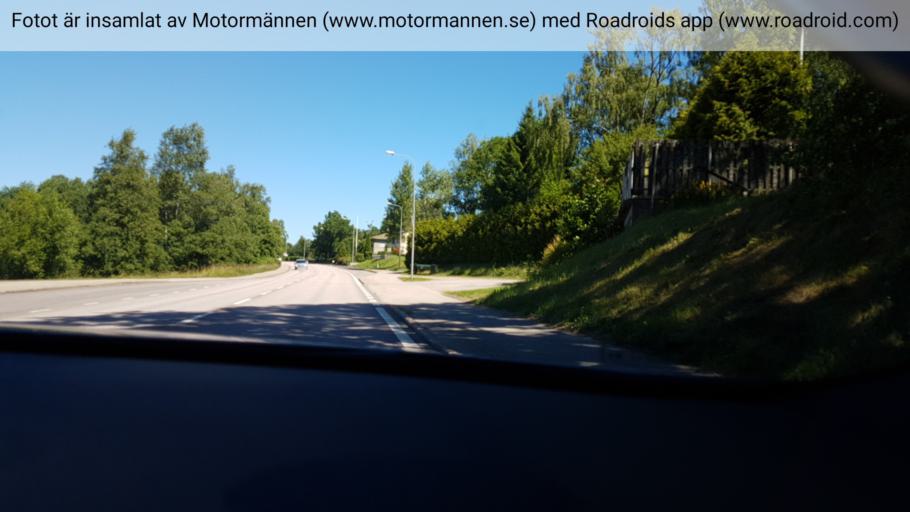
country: SE
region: Vaestra Goetaland
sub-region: Ulricehamns Kommun
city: Ulricehamn
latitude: 57.9004
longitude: 13.4689
